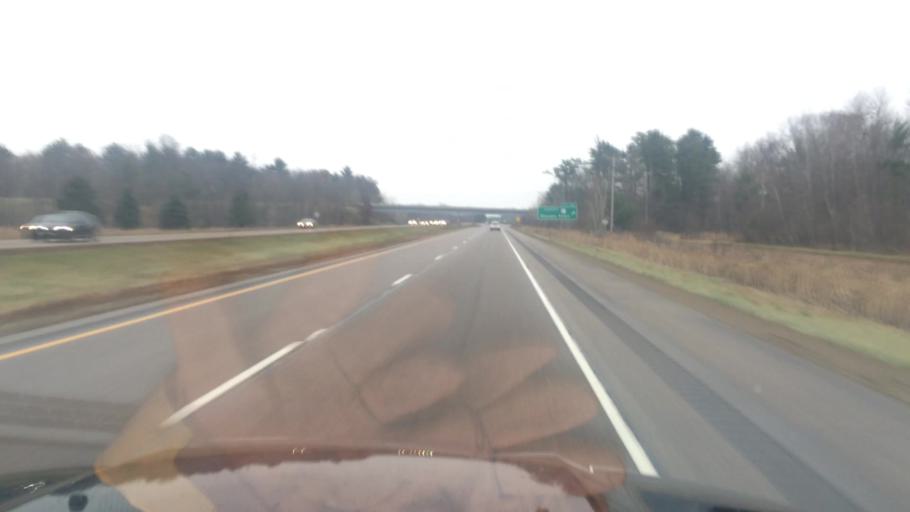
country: US
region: Wisconsin
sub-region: Portage County
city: Stevens Point
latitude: 44.5553
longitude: -89.5863
